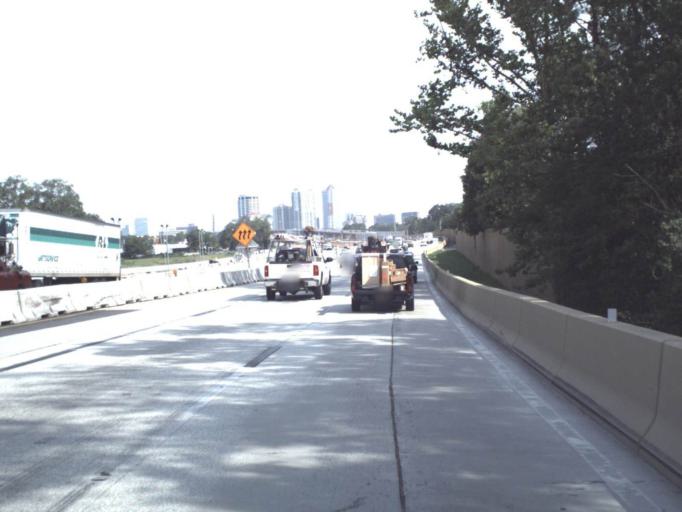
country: US
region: Florida
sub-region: Duval County
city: Jacksonville
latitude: 30.3005
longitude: -81.6398
